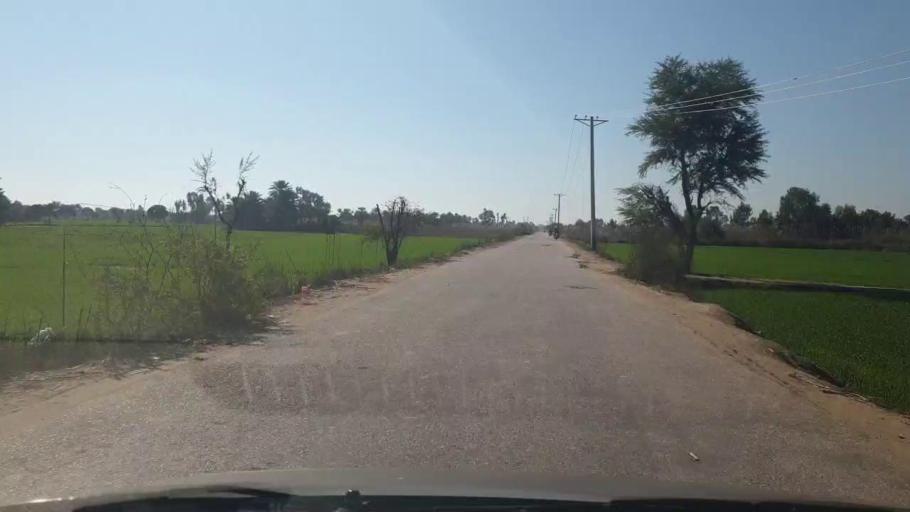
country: PK
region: Sindh
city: Bozdar
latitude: 27.0841
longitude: 68.6213
